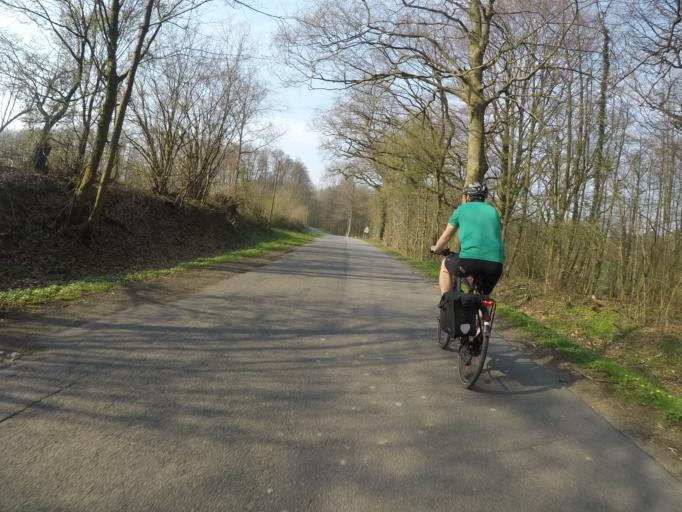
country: DE
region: Schleswig-Holstein
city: Kukels
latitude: 53.8885
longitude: 10.2404
